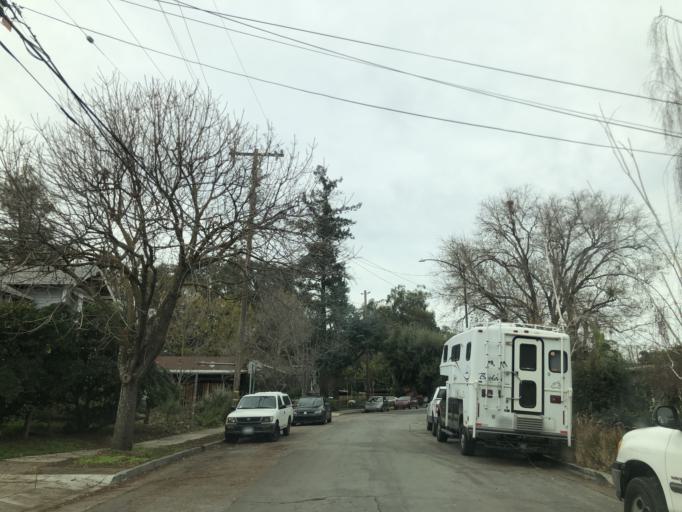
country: US
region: California
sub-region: Santa Clara County
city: San Jose
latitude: 37.3380
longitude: -121.8688
